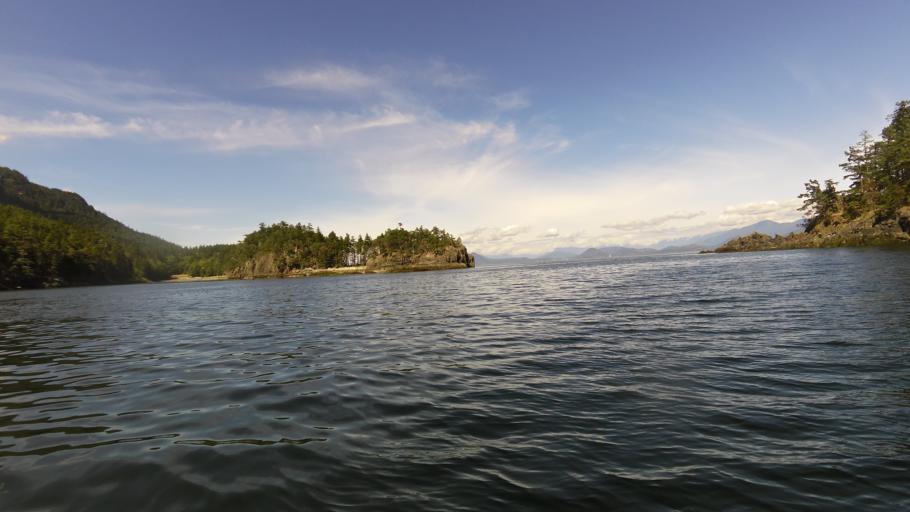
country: CA
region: British Columbia
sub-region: Regional District of Nanaimo
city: Parksville
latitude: 49.5142
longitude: -124.1340
